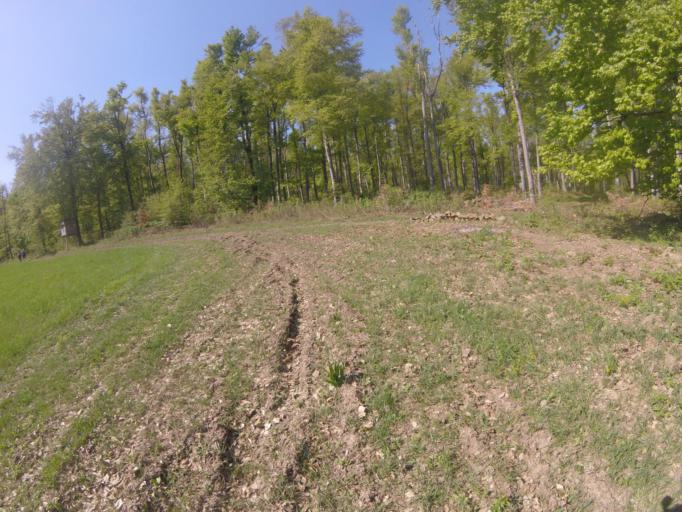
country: HU
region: Pest
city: Pilisszanto
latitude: 47.6985
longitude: 18.8702
